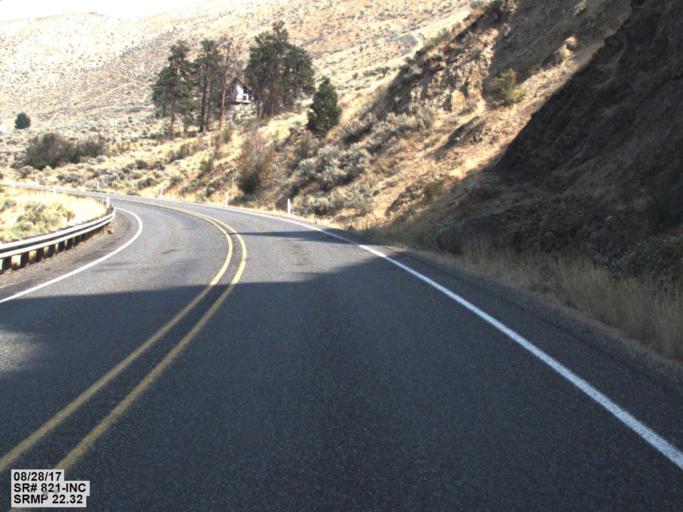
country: US
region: Washington
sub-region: Kittitas County
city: Ellensburg
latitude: 46.8981
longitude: -120.4974
